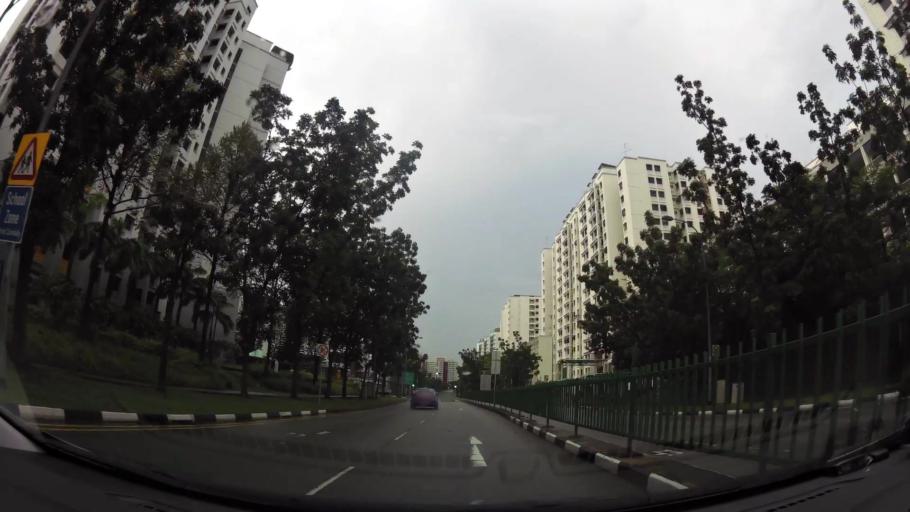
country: MY
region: Johor
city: Kampung Pasir Gudang Baru
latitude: 1.3897
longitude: 103.8917
